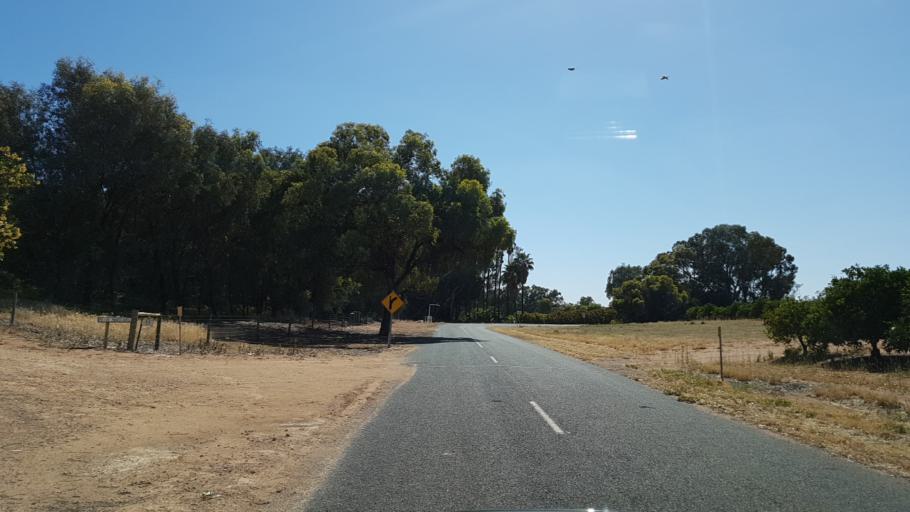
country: AU
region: South Australia
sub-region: Loxton Waikerie
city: Waikerie
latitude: -34.1648
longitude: 140.0304
